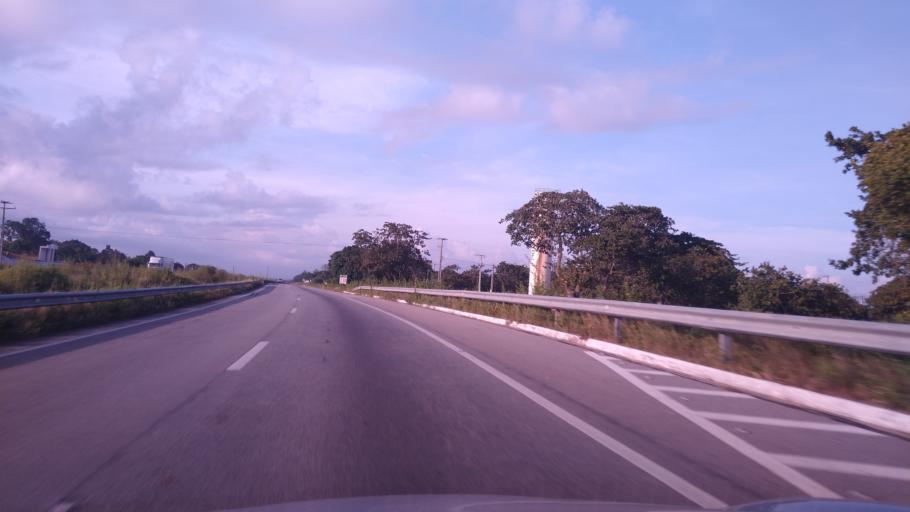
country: BR
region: Ceara
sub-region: Pacajus
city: Pacajus
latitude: -4.1710
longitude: -38.4933
